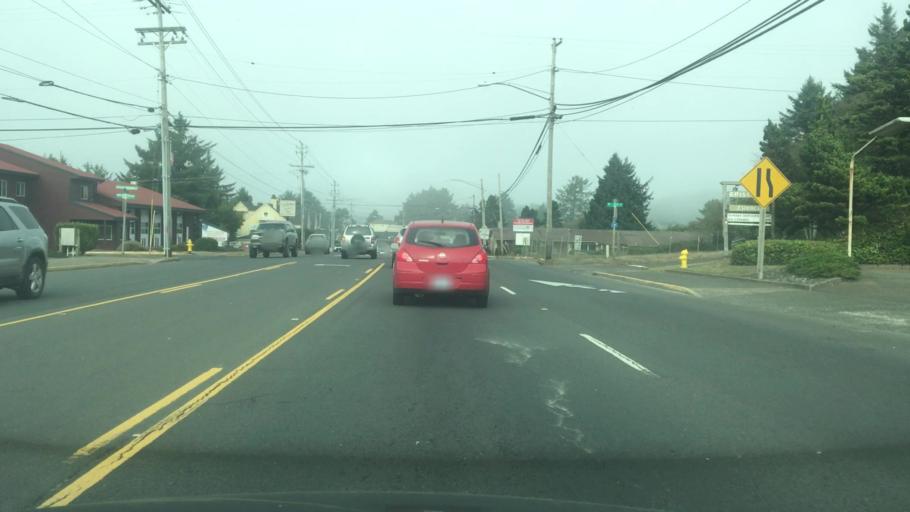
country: US
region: Oregon
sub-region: Lincoln County
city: Lincoln City
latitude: 44.9830
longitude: -124.0072
